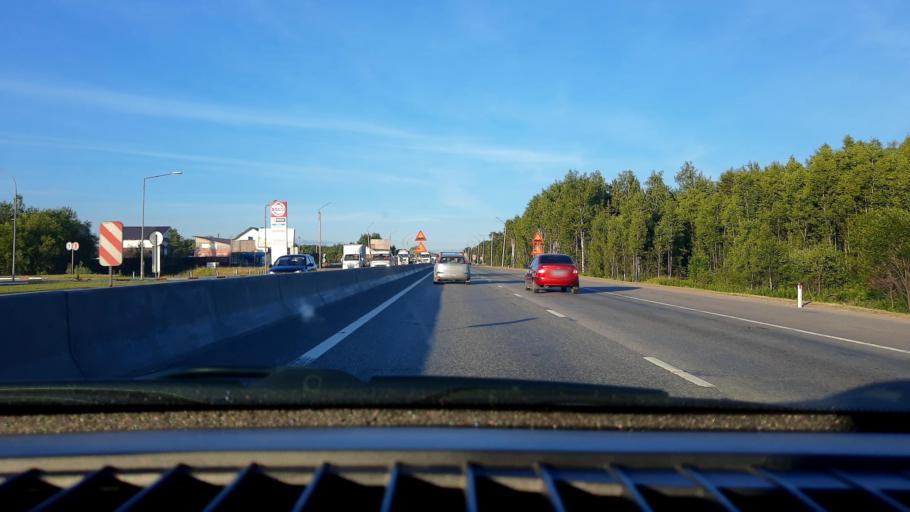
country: RU
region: Nizjnij Novgorod
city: Babino
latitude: 56.3040
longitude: 43.6079
